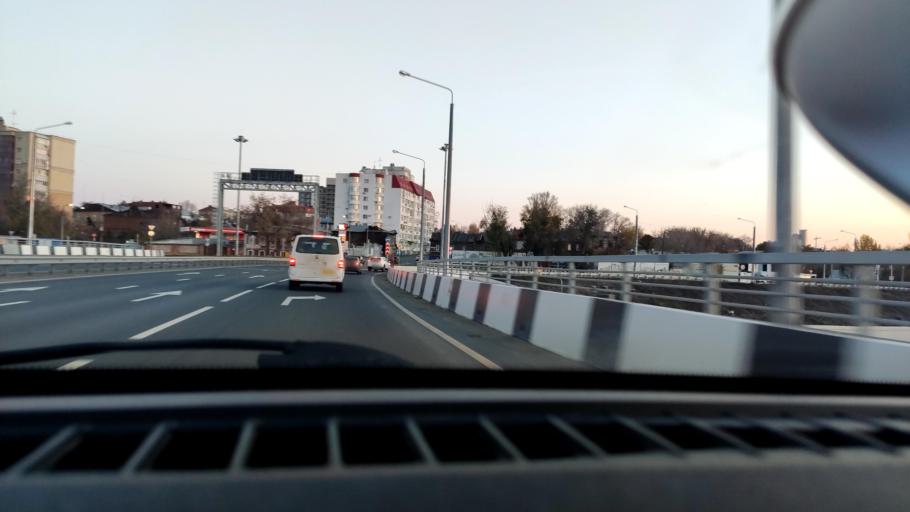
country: RU
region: Samara
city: Rozhdestveno
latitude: 53.1774
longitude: 50.0856
